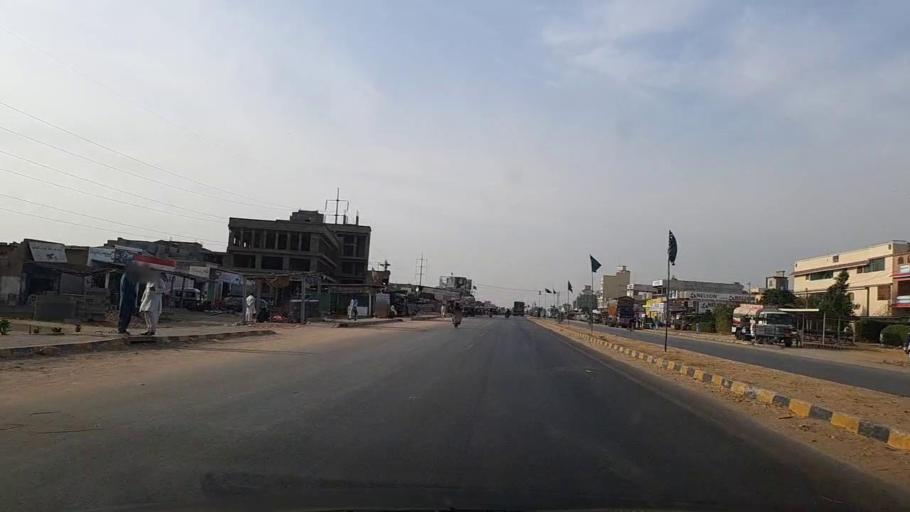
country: PK
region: Sindh
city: Gharo
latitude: 24.7897
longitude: 67.5266
